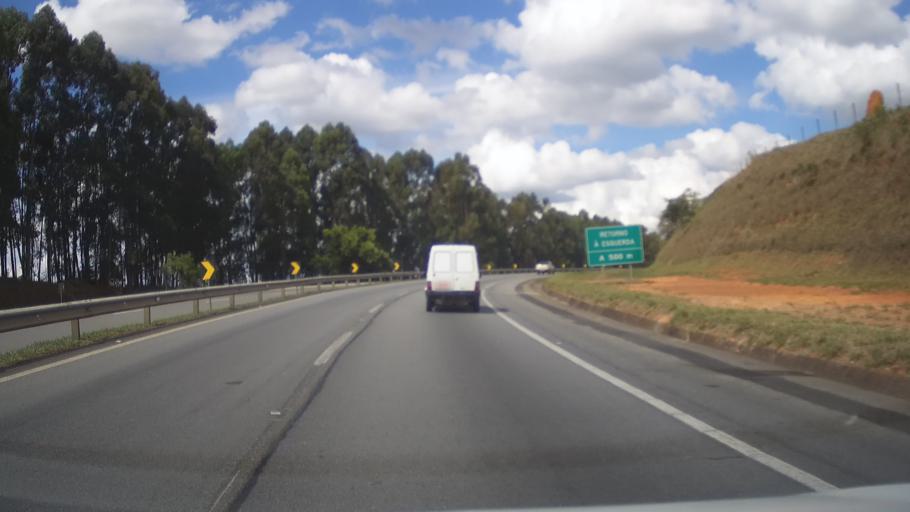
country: BR
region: Minas Gerais
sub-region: Oliveira
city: Oliveira
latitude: -20.8297
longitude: -44.8173
